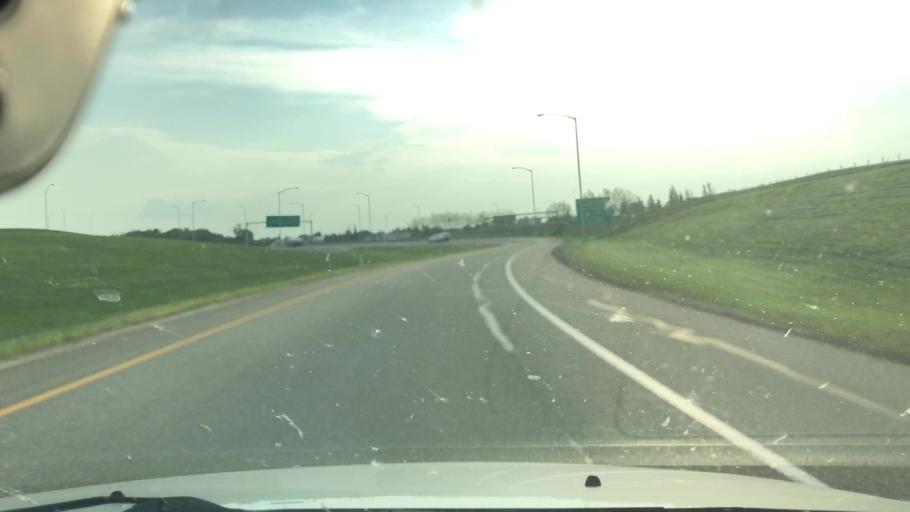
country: CA
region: Alberta
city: St. Albert
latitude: 53.6194
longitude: -113.5986
